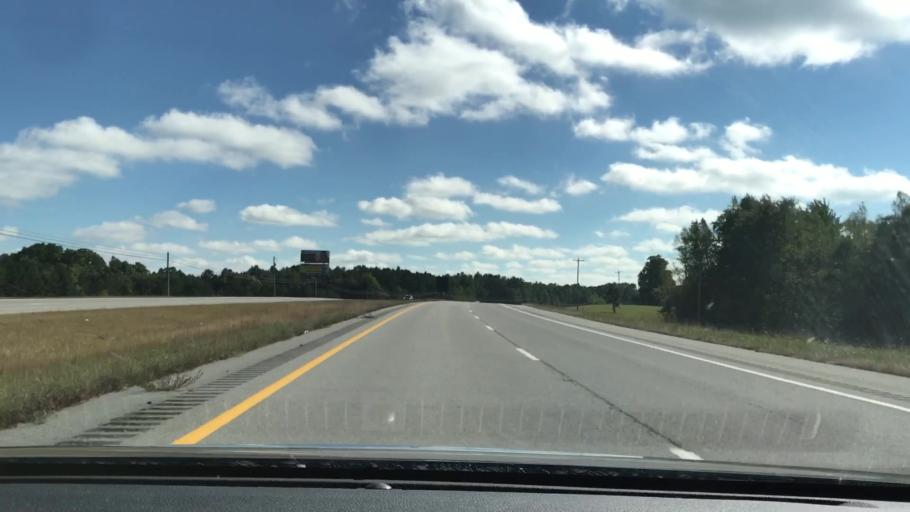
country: US
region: Tennessee
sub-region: Fentress County
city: Grimsley
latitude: 36.3438
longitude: -84.9525
